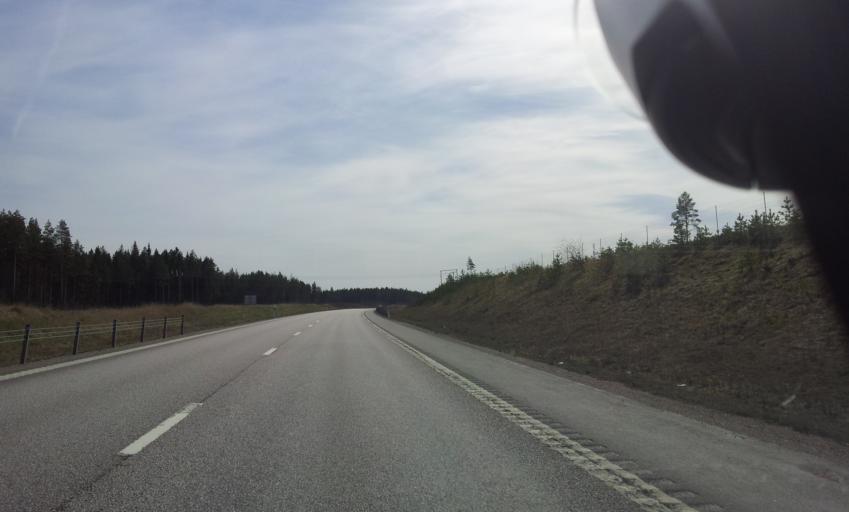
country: SE
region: Uppsala
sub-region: Tierps Kommun
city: Tierp
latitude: 60.3145
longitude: 17.5202
